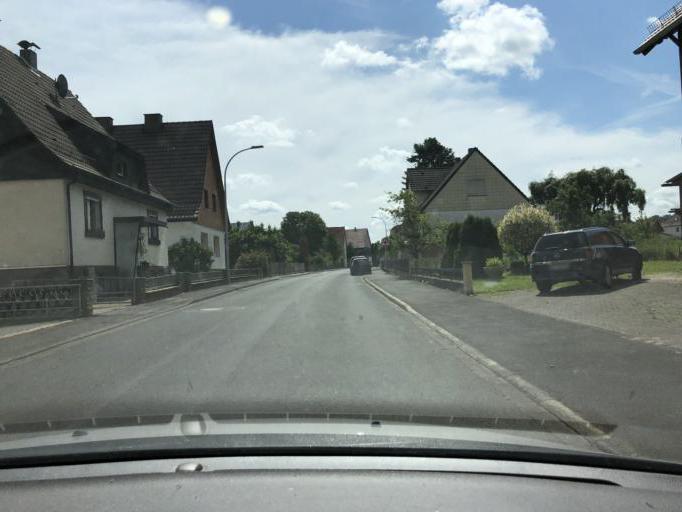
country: DE
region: Hesse
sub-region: Regierungsbezirk Kassel
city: Alheim
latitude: 51.0426
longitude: 9.6521
